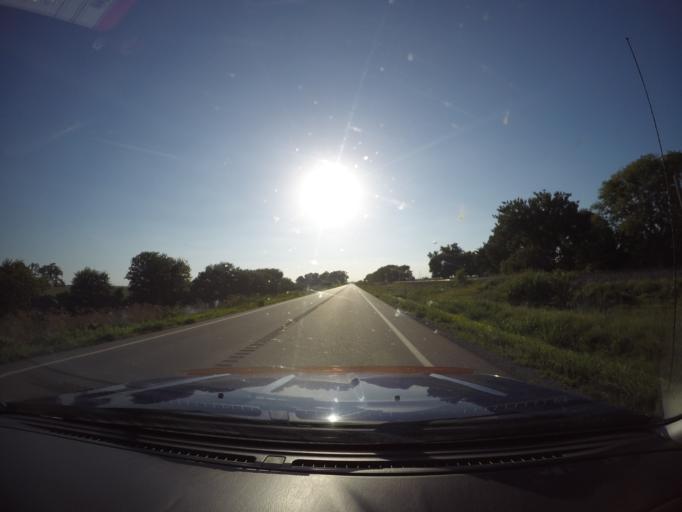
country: US
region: Kansas
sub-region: Shawnee County
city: Rossville
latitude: 39.1171
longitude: -95.9067
